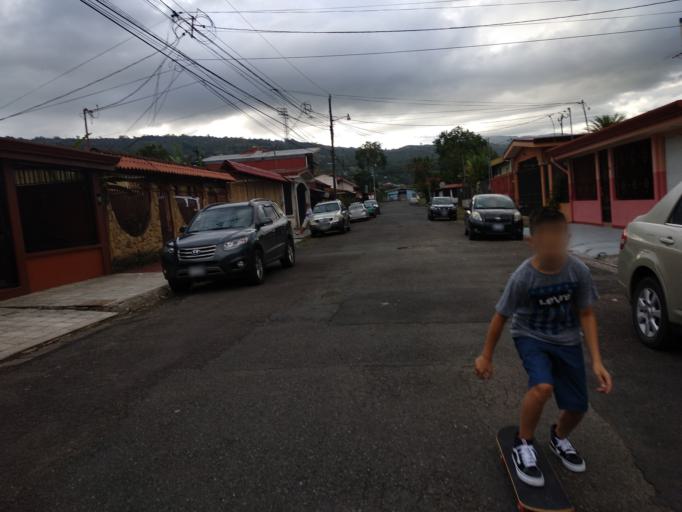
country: CR
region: Cartago
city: Turrialba
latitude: 9.8997
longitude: -83.6741
